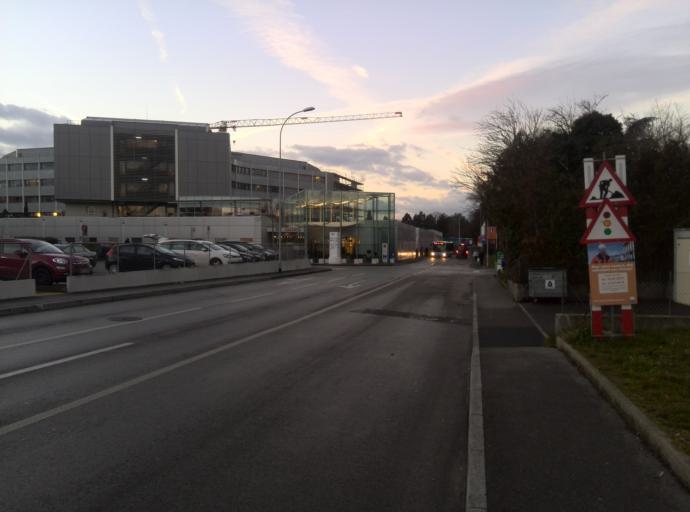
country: CH
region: Geneva
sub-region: Geneva
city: Meyrin
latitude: 46.2299
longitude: 6.0676
